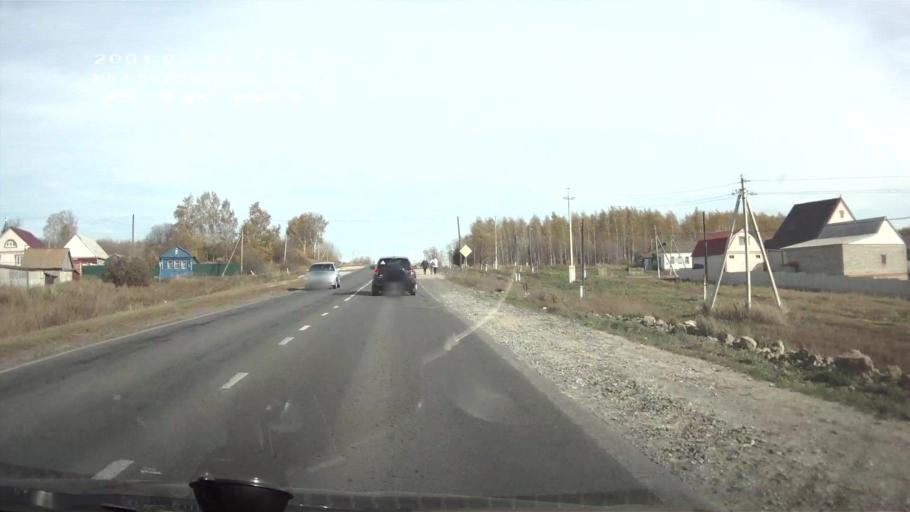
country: RU
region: Mordoviya
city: Atyashevo
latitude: 54.5626
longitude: 45.9809
